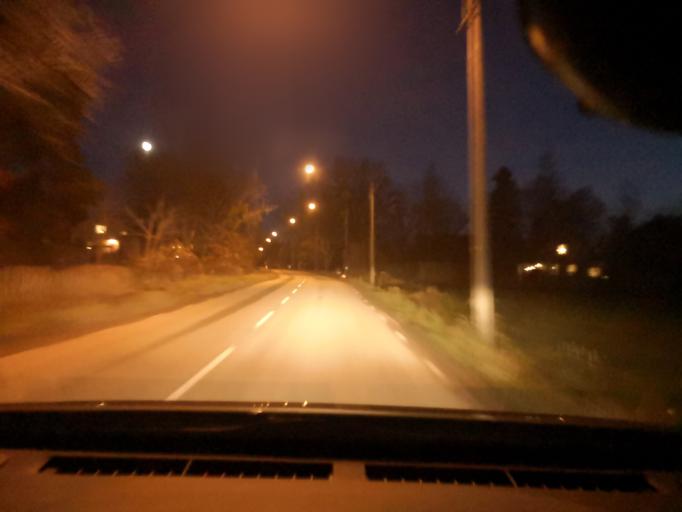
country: SE
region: OErebro
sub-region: Orebro Kommun
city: Orebro
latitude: 59.2537
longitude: 15.2744
